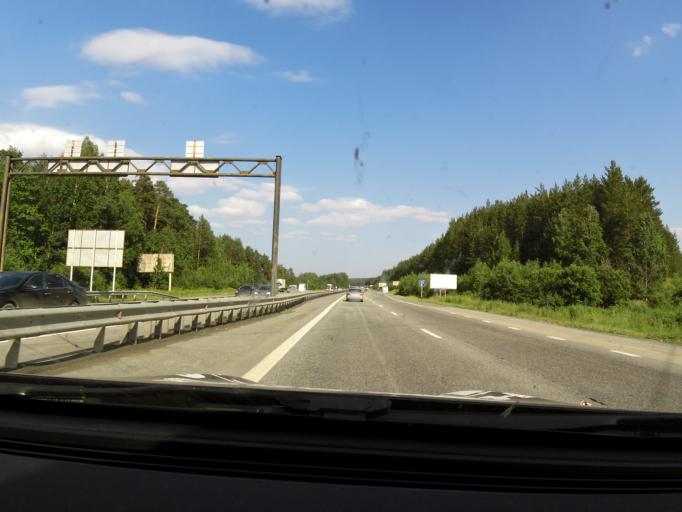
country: RU
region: Sverdlovsk
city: Severka
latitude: 56.8328
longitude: 60.3299
